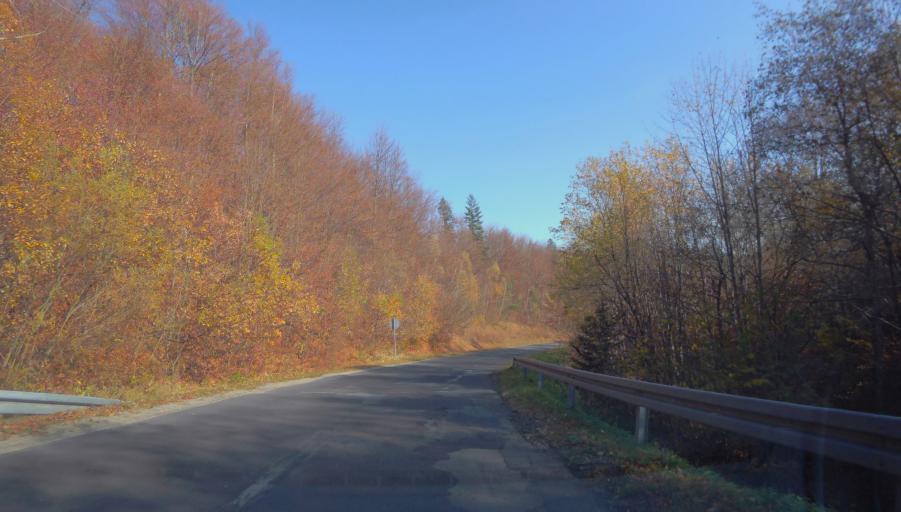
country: PL
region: Subcarpathian Voivodeship
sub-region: Powiat leski
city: Cisna
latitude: 49.2092
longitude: 22.2432
